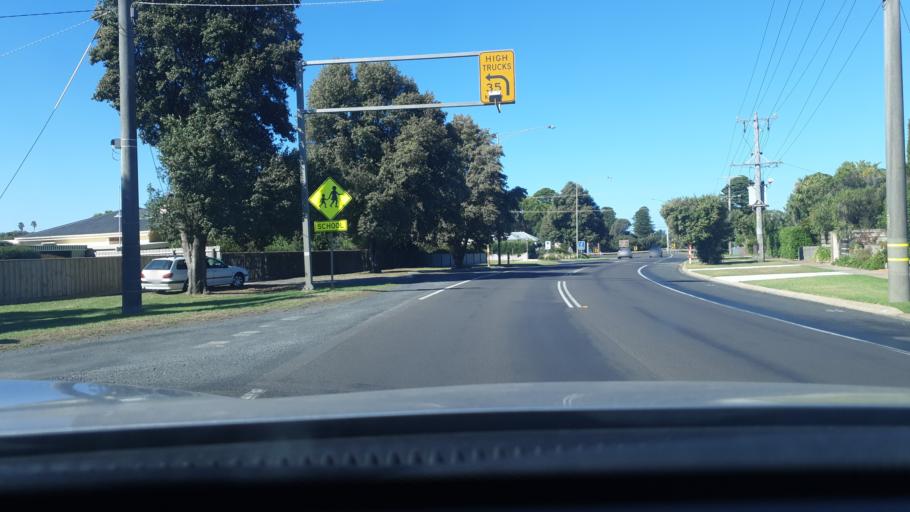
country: AU
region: Victoria
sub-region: Moyne
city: Port Fairy
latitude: -38.3846
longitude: 142.2263
